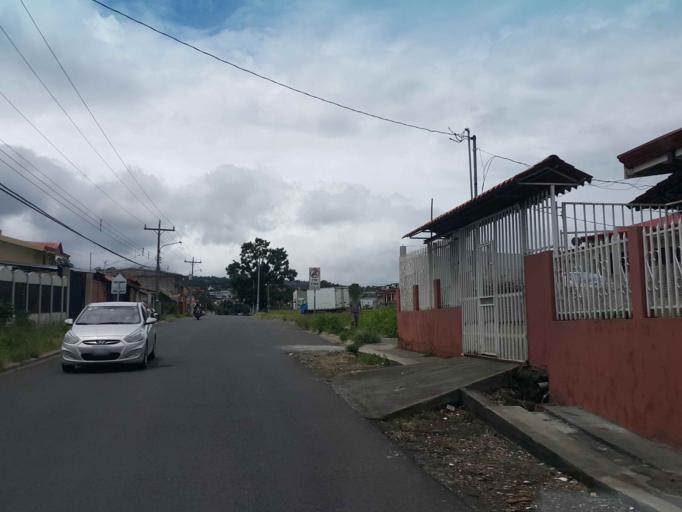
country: CR
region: Heredia
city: Heredia
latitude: 10.0124
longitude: -84.1171
